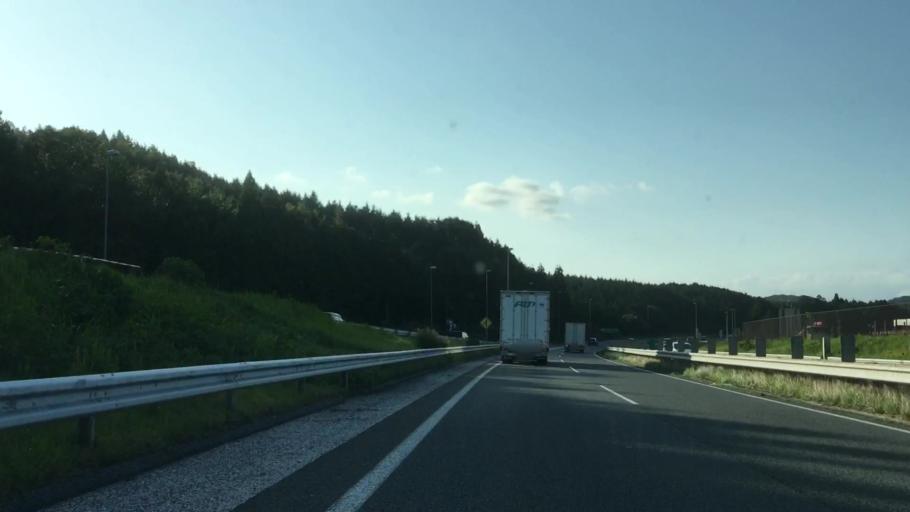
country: JP
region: Yamaguchi
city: Ogori-shimogo
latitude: 34.1538
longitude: 131.3367
